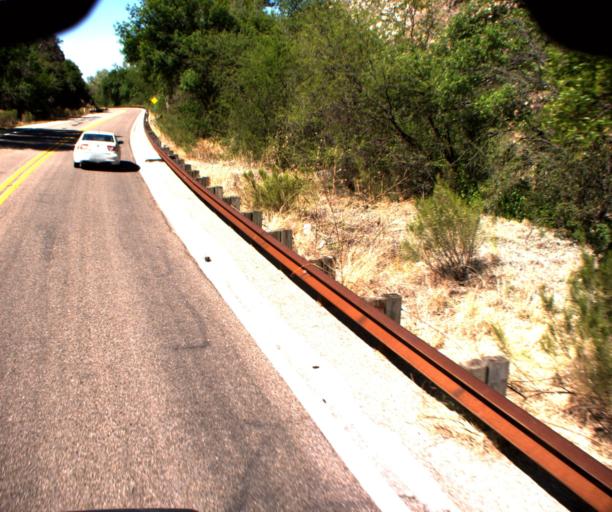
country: US
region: Arizona
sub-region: Santa Cruz County
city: Rio Rico
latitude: 31.5111
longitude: -110.7991
